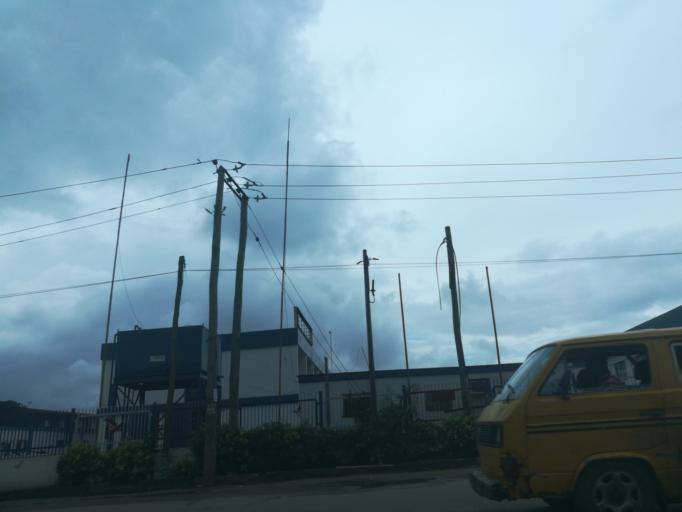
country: NG
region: Lagos
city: Ikeja
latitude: 6.6076
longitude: 3.3363
